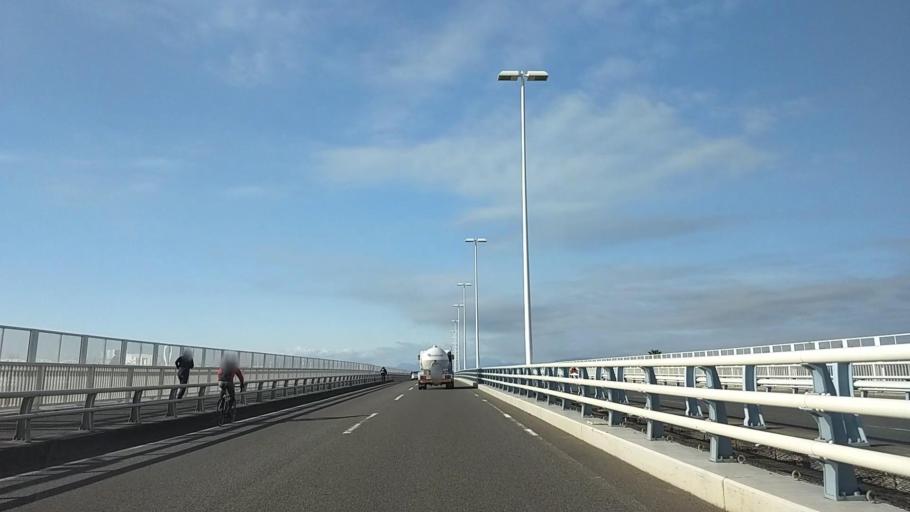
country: JP
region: Kanagawa
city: Hiratsuka
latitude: 35.3191
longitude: 139.3722
